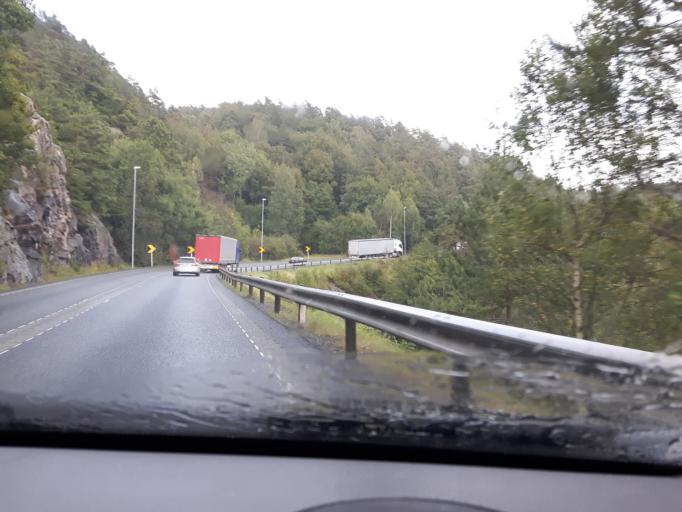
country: NO
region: Vest-Agder
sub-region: Sogne
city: Sogne
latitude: 58.0959
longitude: 7.6869
